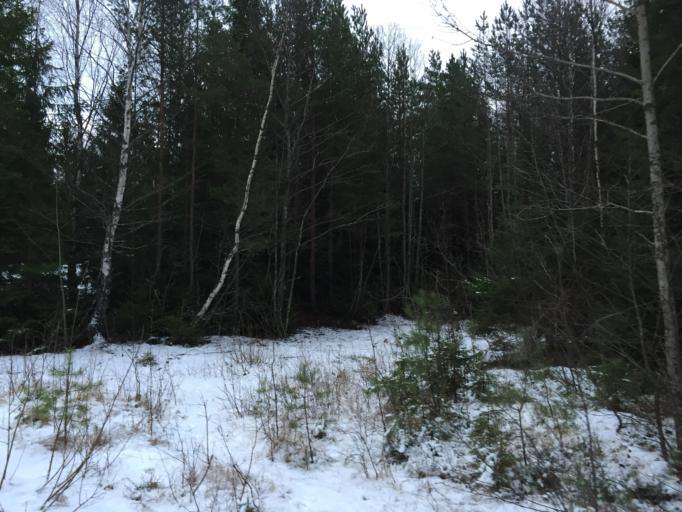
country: SE
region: Stockholm
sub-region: Salems Kommun
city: Ronninge
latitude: 59.2267
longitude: 17.6921
